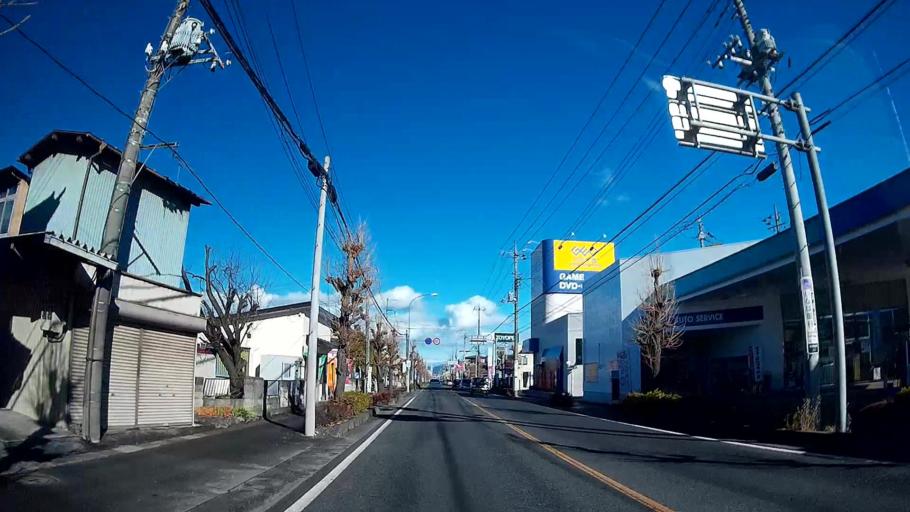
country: JP
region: Saitama
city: Chichibu
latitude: 36.0067
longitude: 139.0916
